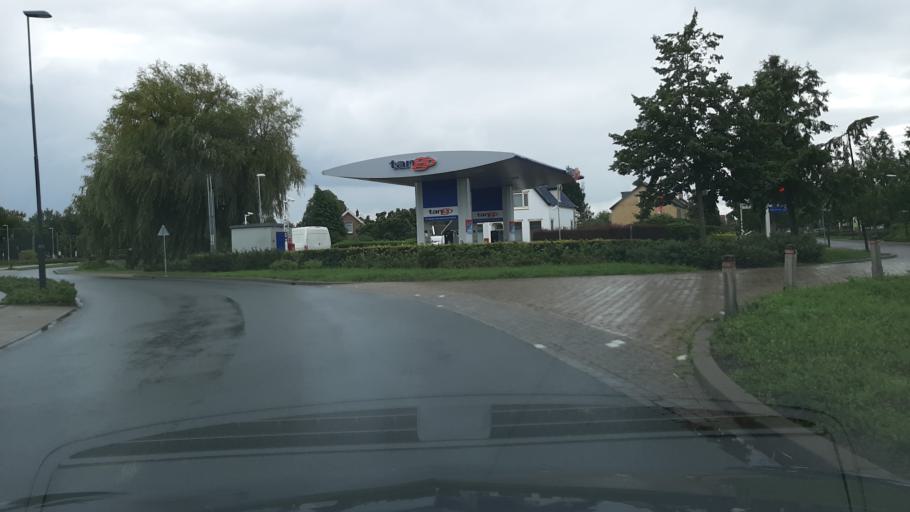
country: NL
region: Friesland
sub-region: Gemeente Weststellingwerf
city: Wolvega
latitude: 52.8821
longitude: 6.0010
